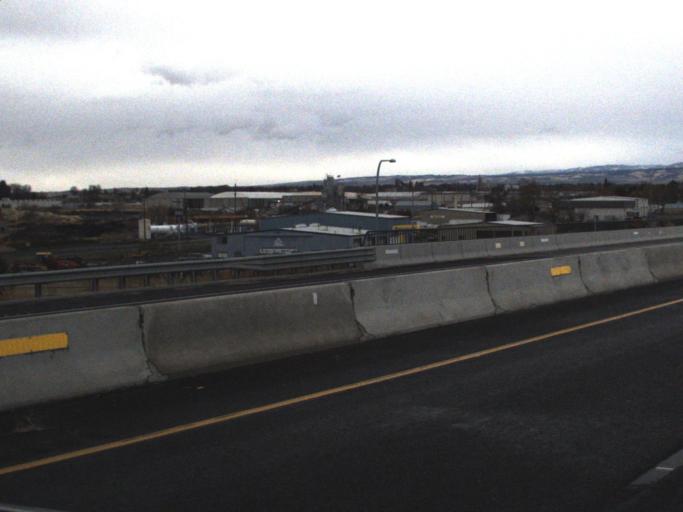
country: US
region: Washington
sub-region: Walla Walla County
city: Walla Walla
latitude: 46.0697
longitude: -118.3698
